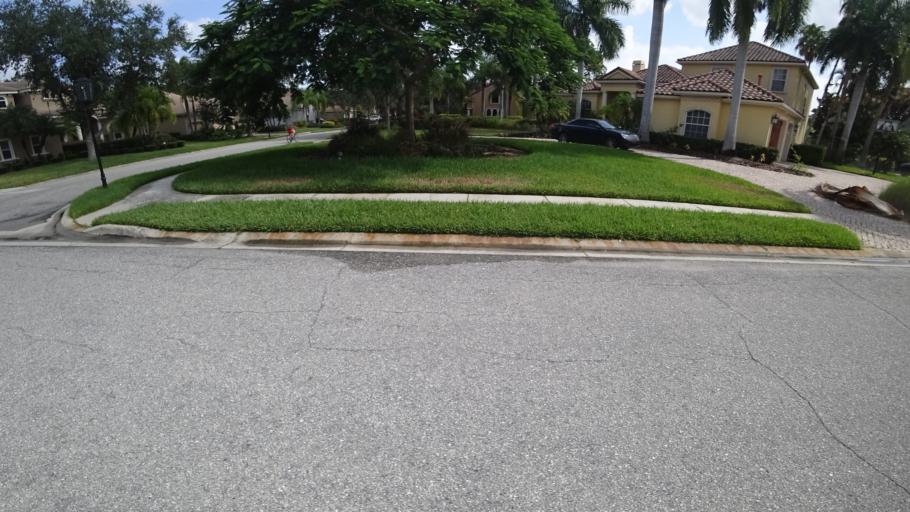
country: US
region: Florida
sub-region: Sarasota County
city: The Meadows
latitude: 27.3997
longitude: -82.4462
